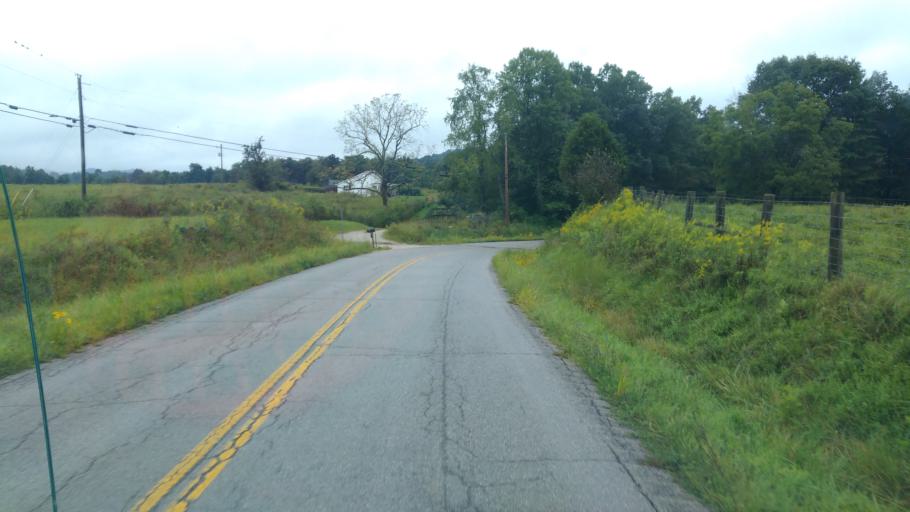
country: US
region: Kentucky
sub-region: Fleming County
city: Flemingsburg
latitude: 38.4549
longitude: -83.5211
